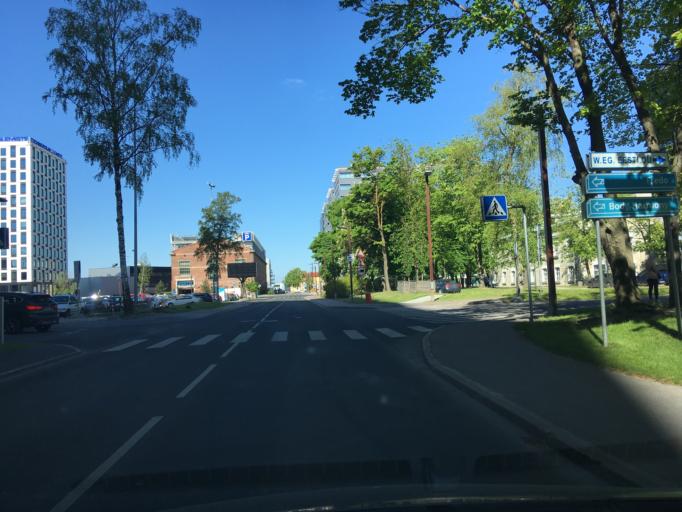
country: EE
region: Harju
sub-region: Tallinna linn
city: Tallinn
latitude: 59.4204
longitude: 24.8046
